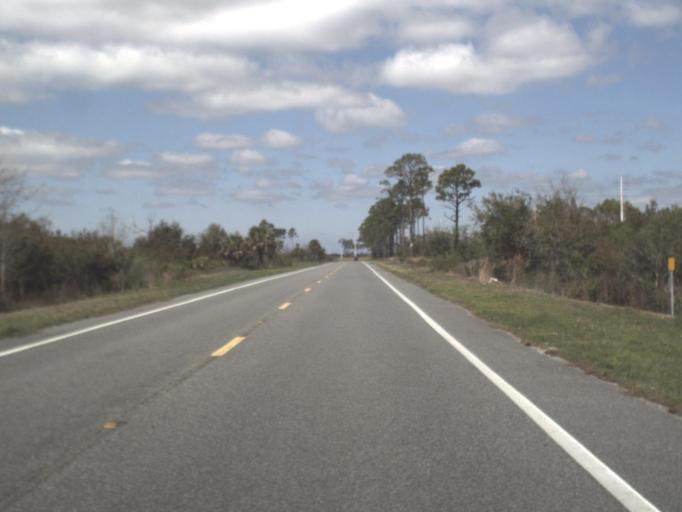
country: US
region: Florida
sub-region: Franklin County
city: Apalachicola
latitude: 29.7218
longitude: -85.0711
